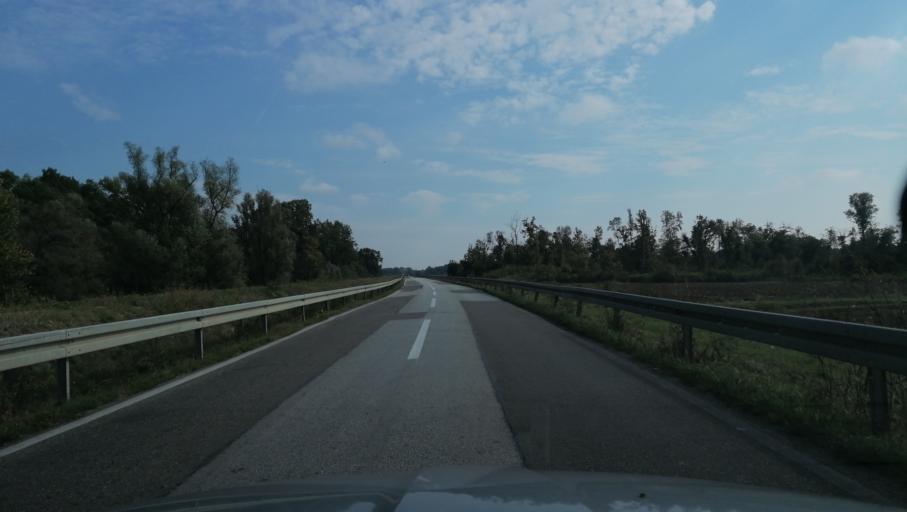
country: BA
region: Republika Srpska
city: Balatun
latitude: 44.9012
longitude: 19.3078
